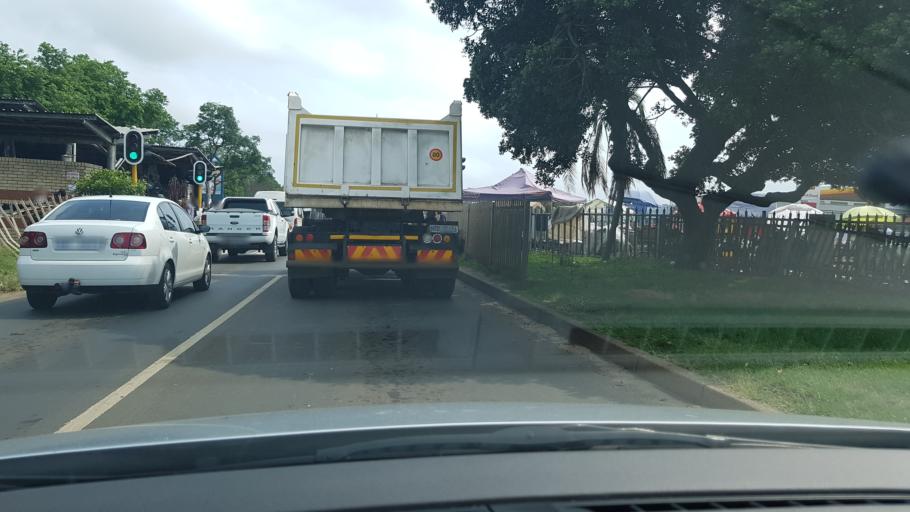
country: ZA
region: KwaZulu-Natal
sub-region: uThungulu District Municipality
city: Richards Bay
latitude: -28.7510
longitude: 32.0481
